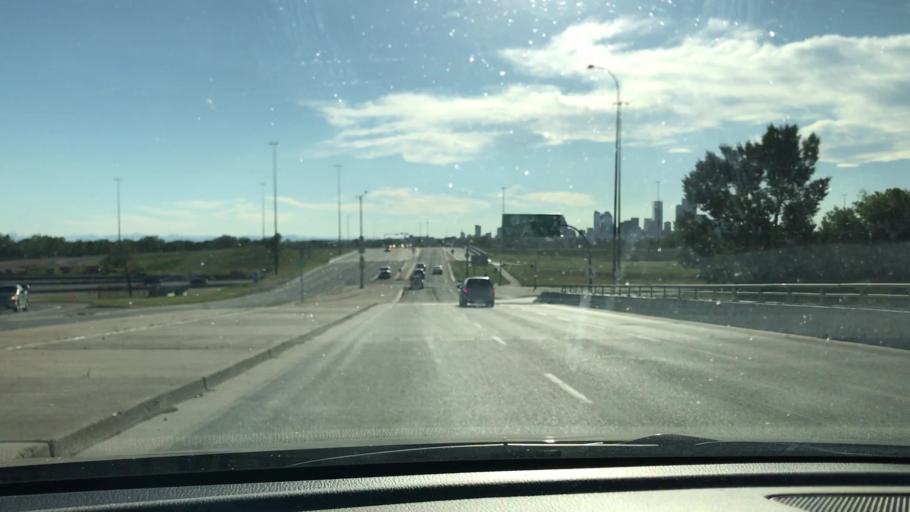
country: CA
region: Alberta
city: Calgary
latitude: 51.0371
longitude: -114.0009
